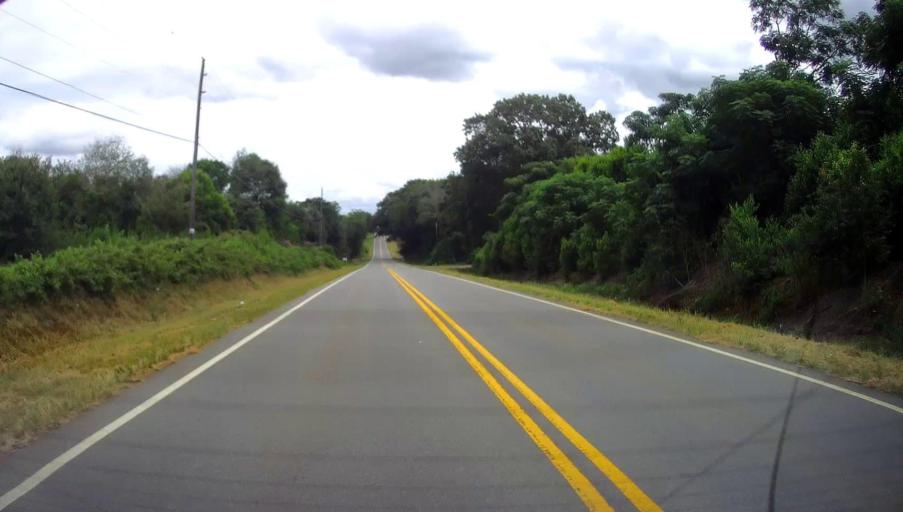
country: US
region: Georgia
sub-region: Macon County
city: Montezuma
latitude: 32.2932
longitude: -83.9941
